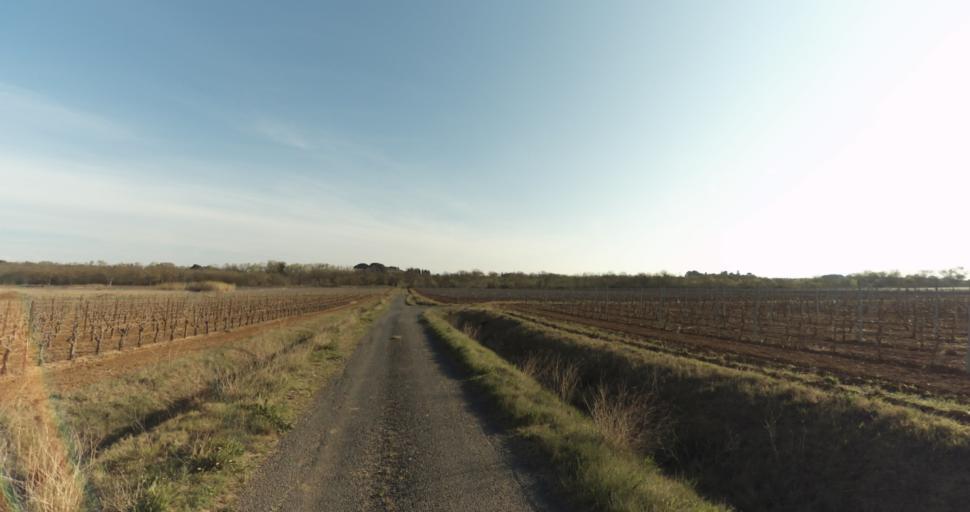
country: FR
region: Languedoc-Roussillon
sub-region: Departement de l'Herault
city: Marseillan
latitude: 43.3822
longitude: 3.5325
